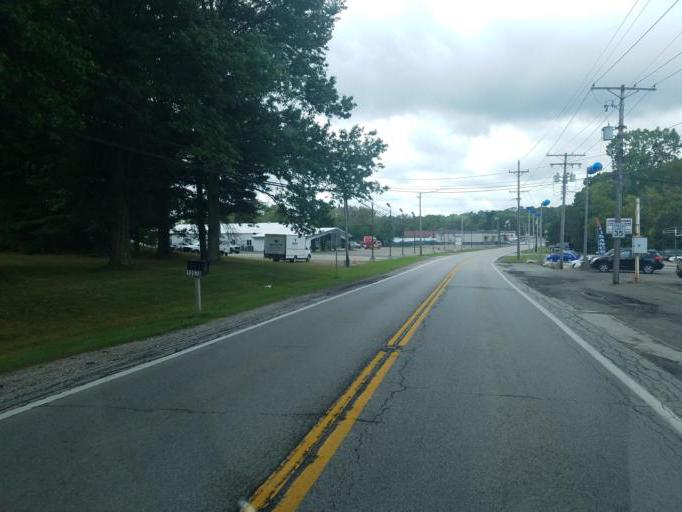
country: US
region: Ohio
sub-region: Geauga County
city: Chardon
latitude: 41.5852
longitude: -81.1869
